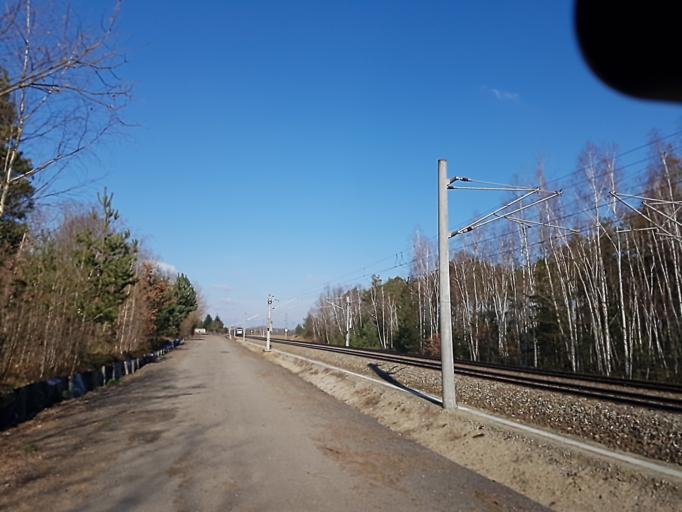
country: DE
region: Brandenburg
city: Ruckersdorf
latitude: 51.6042
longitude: 13.5650
